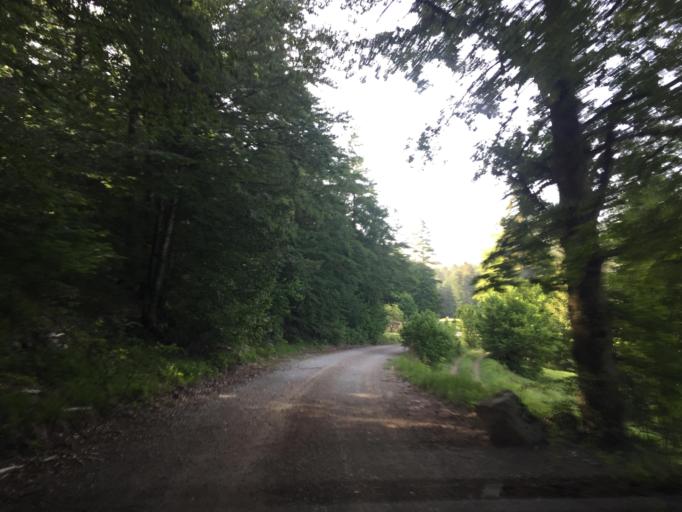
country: HR
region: Primorsko-Goranska
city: Klana
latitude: 45.4915
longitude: 14.4571
